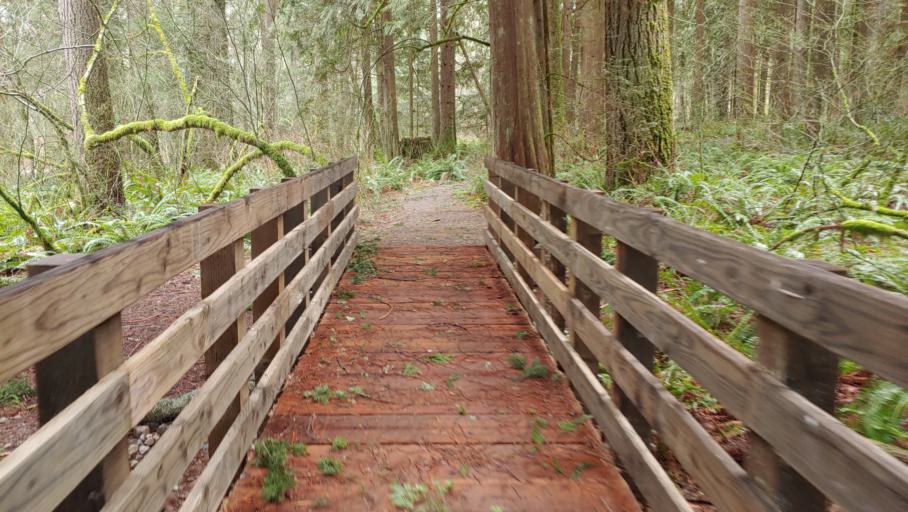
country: US
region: Washington
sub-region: King County
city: Hobart
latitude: 47.4676
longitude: -121.9331
